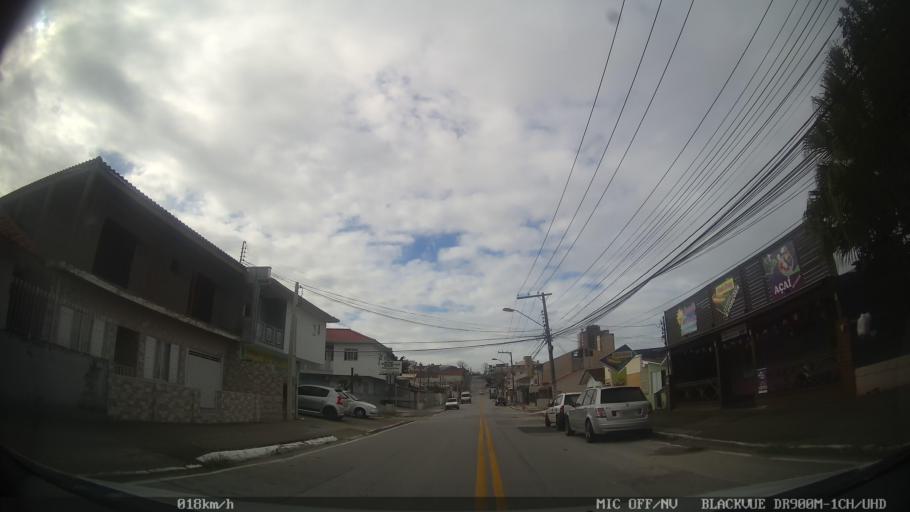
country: BR
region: Santa Catarina
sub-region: Sao Jose
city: Campinas
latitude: -27.5741
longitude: -48.6216
